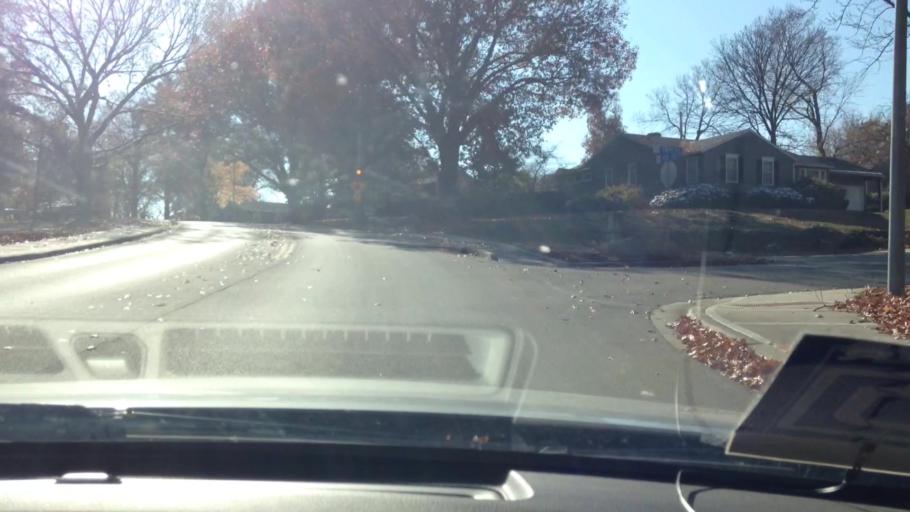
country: US
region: Kansas
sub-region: Johnson County
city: Prairie Village
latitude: 38.9877
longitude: -94.6392
